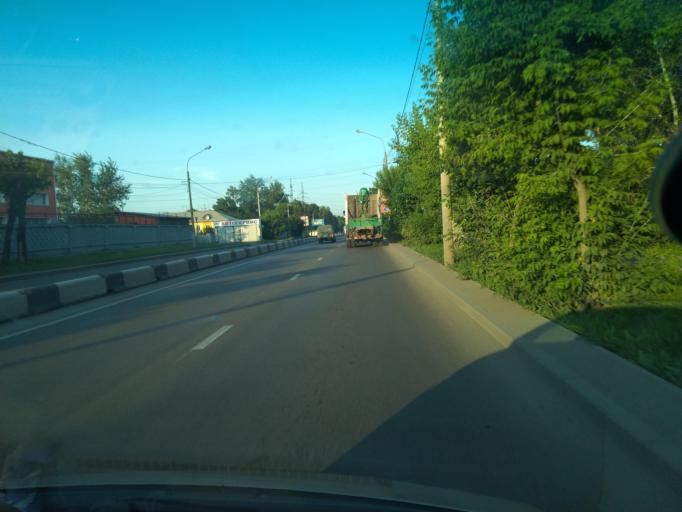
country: RU
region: Krasnoyarskiy
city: Berezovka
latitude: 56.0213
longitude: 93.0428
